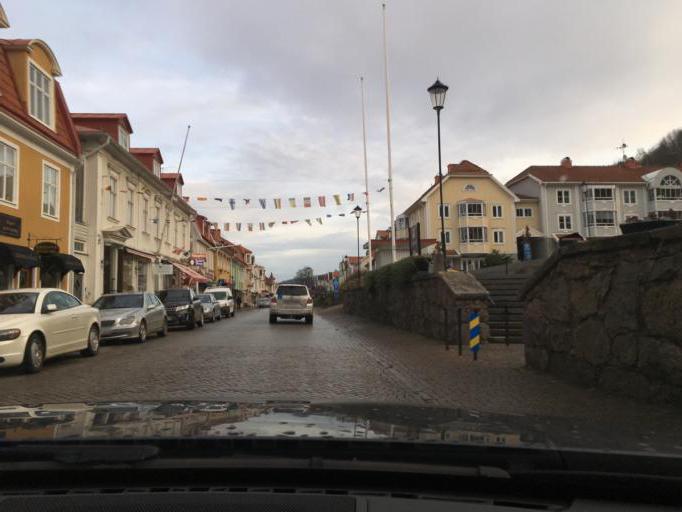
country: SE
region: Joenkoeping
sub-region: Jonkopings Kommun
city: Graenna
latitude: 58.0227
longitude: 14.4674
